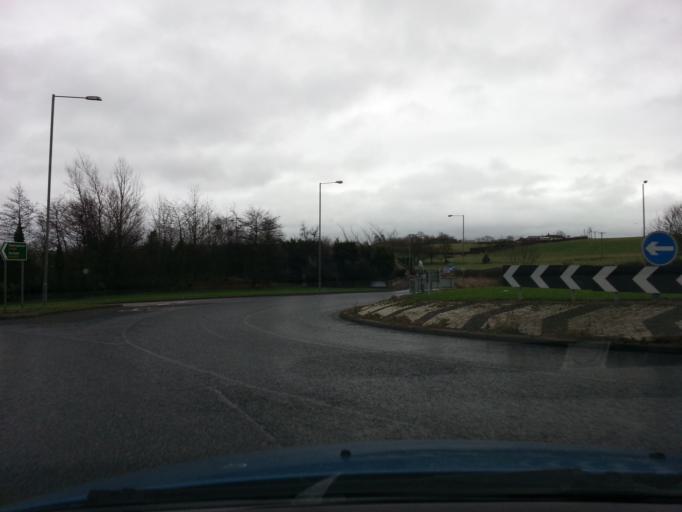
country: GB
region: England
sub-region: County Durham
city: Bishop Auckland
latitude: 54.6626
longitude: -1.6485
